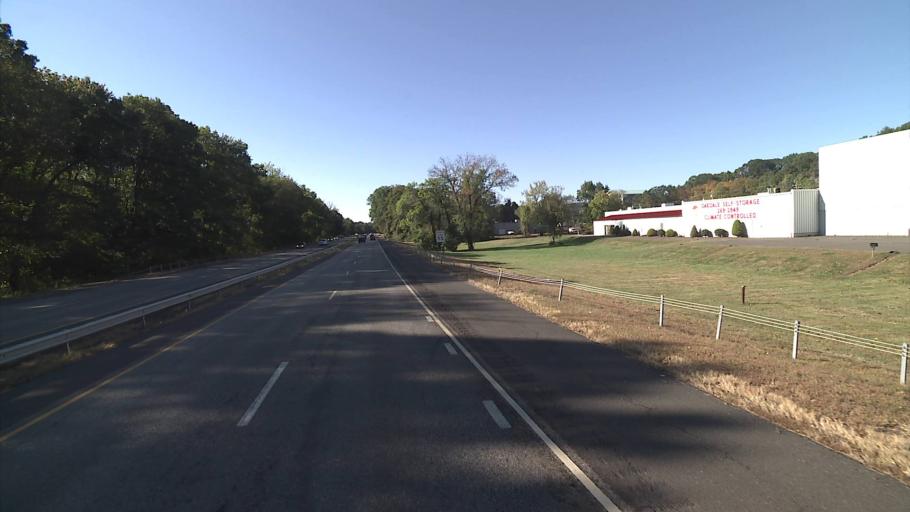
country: US
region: Connecticut
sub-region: New Haven County
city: Wallingford
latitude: 41.4531
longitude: -72.8405
